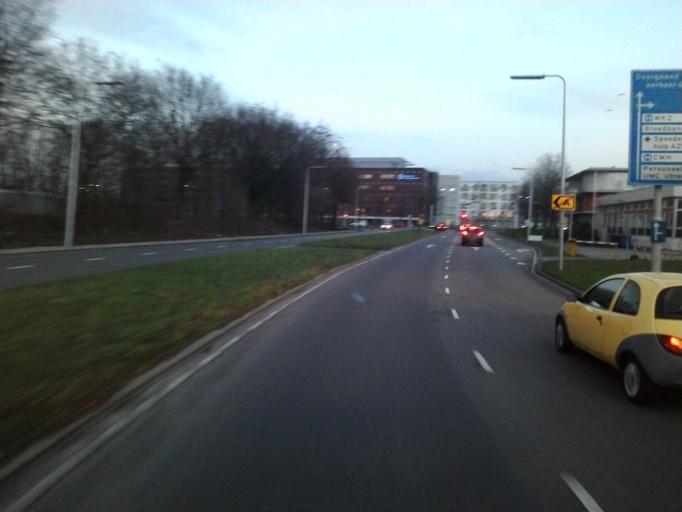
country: NL
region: Utrecht
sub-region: Gemeente De Bilt
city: De Bilt
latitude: 52.0890
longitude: 5.1773
